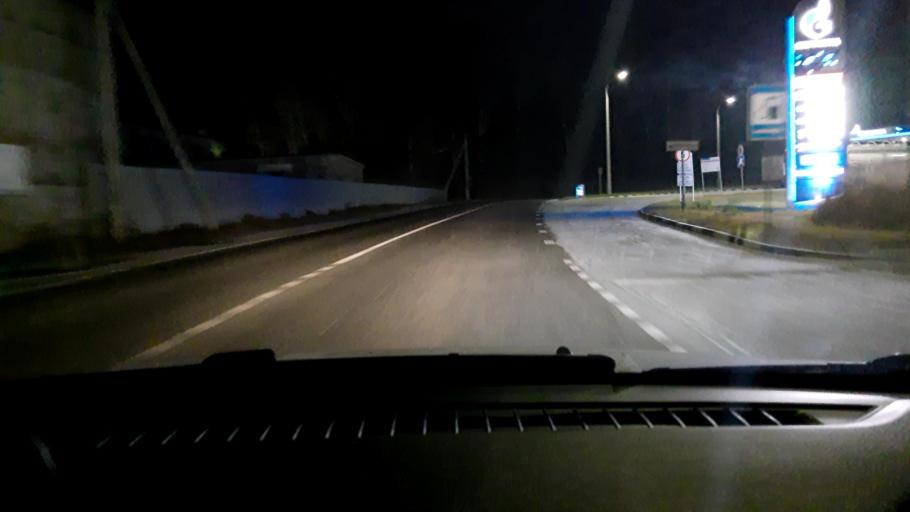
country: RU
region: Nizjnij Novgorod
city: Novaya Balakhna
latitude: 56.5061
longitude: 43.5919
